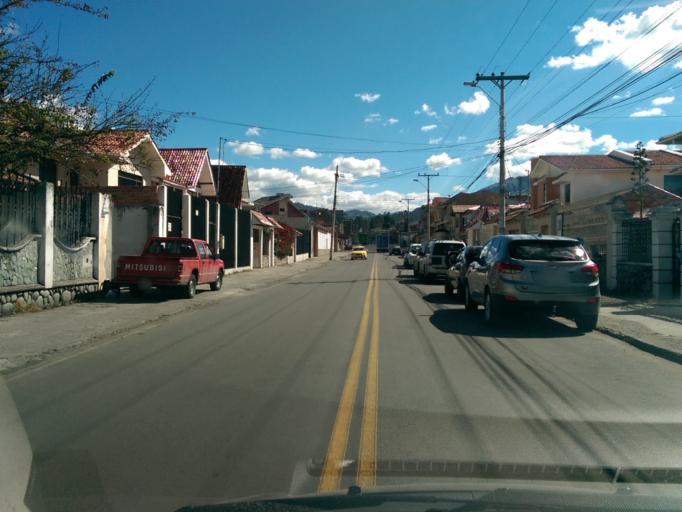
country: EC
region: Azuay
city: Cuenca
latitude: -2.9016
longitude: -79.0189
